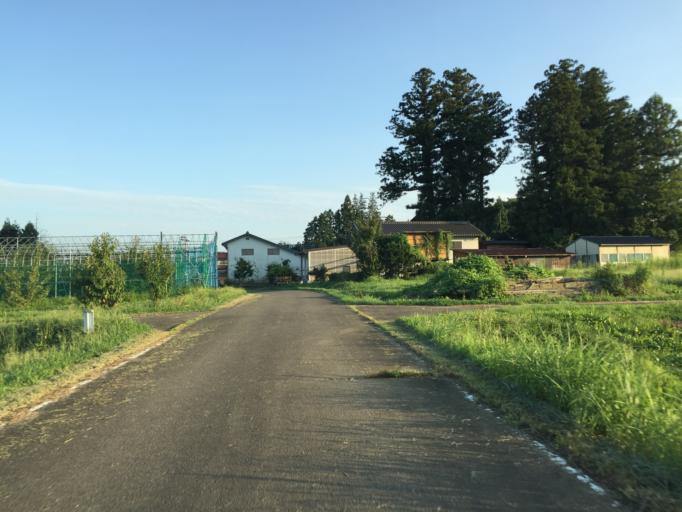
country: JP
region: Fukushima
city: Fukushima-shi
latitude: 37.7275
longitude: 140.3774
